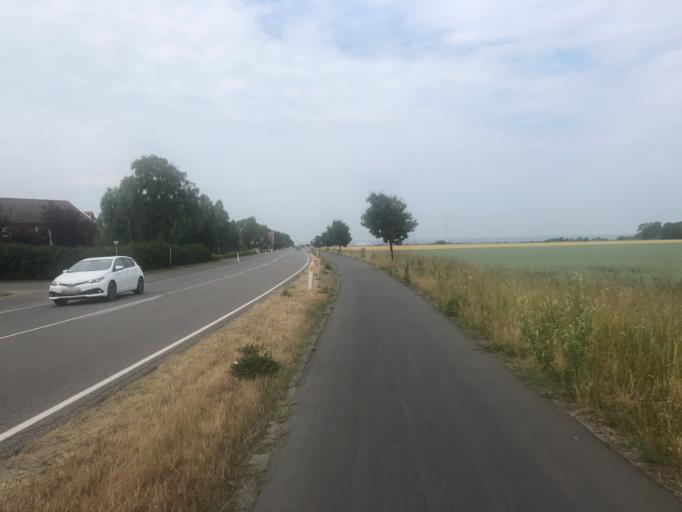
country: DK
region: Capital Region
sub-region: Bornholm Kommune
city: Ronne
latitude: 55.1092
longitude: 14.7462
